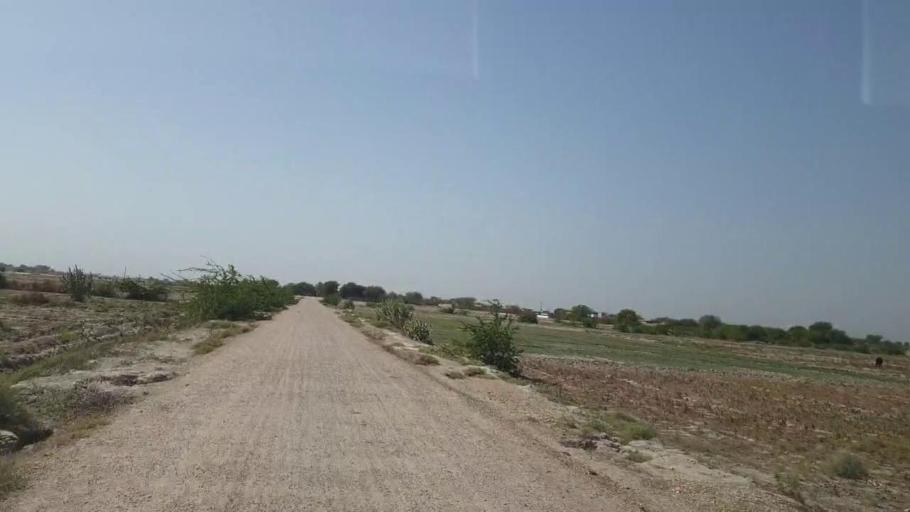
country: PK
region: Sindh
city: Naukot
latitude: 24.9104
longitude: 69.5095
